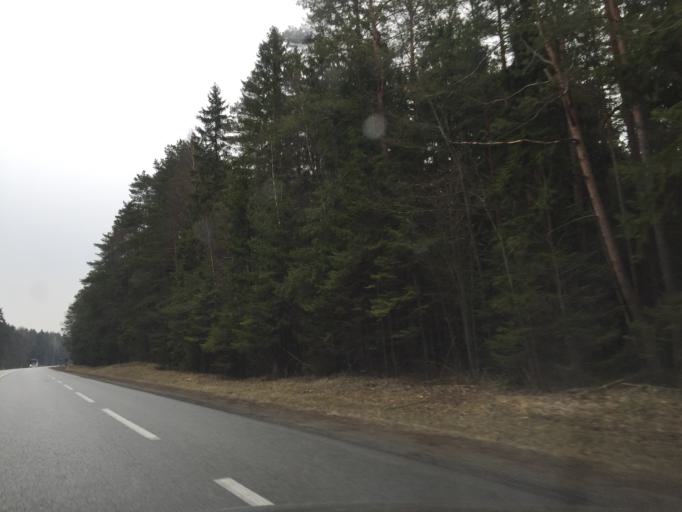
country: LV
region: Saulkrastu
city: Saulkrasti
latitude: 57.4480
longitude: 24.4298
